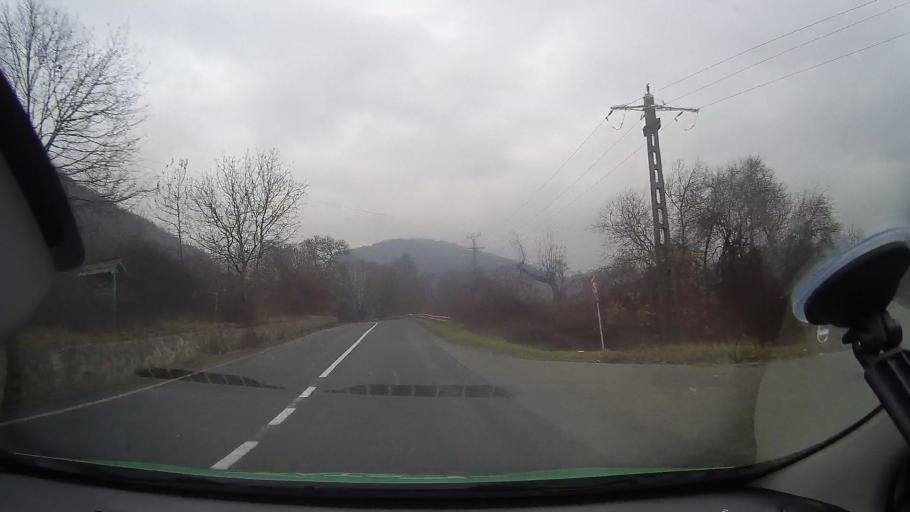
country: RO
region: Arad
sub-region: Comuna Plescuta
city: Plescuta
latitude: 46.2951
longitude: 22.4366
